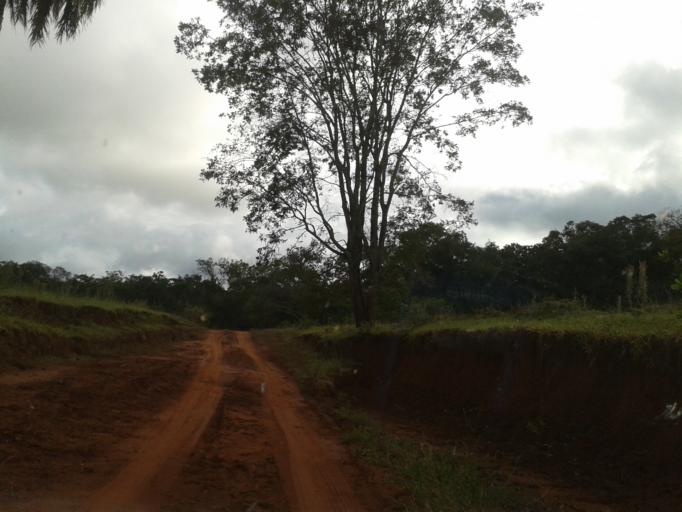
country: BR
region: Minas Gerais
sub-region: Campina Verde
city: Campina Verde
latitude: -19.4969
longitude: -49.6060
